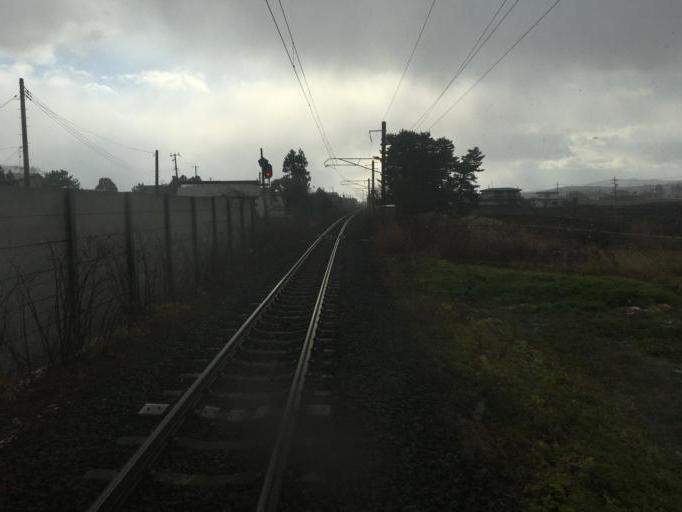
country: JP
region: Aomori
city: Aomori Shi
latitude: 40.9728
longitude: 140.6545
